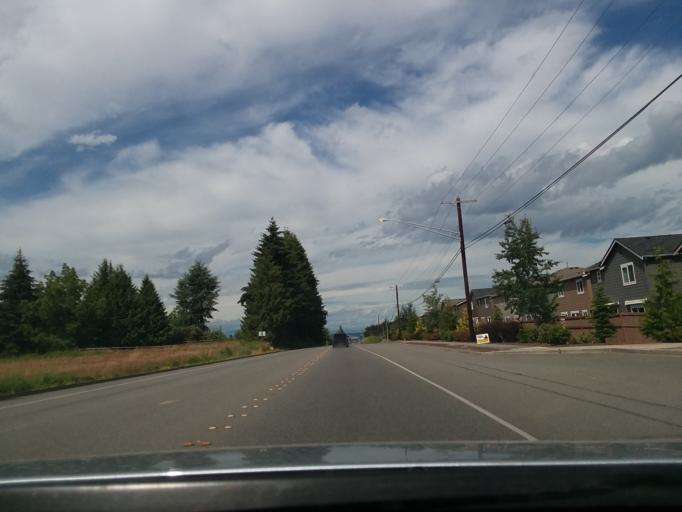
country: US
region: Washington
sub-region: Snohomish County
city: West Lake Stevens
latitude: 47.9781
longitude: -122.1255
